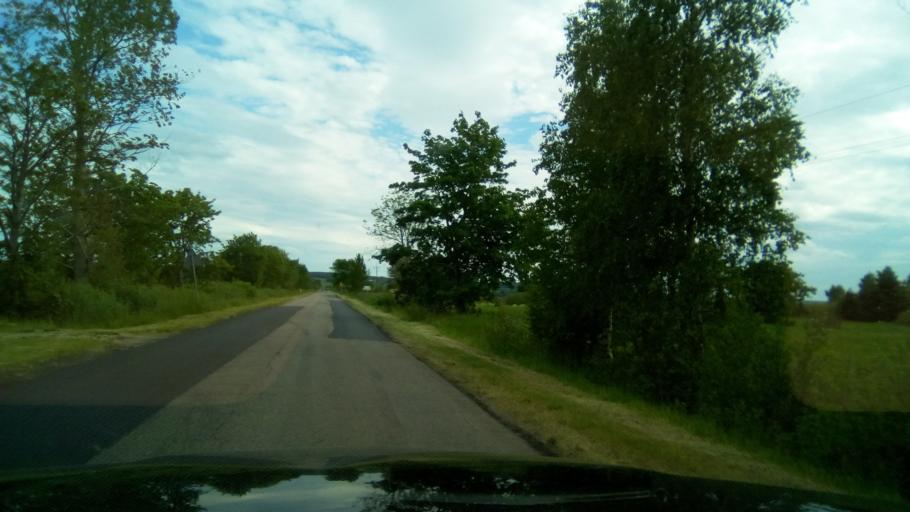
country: PL
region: Pomeranian Voivodeship
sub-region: Powiat pucki
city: Krokowa
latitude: 54.8193
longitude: 18.0870
